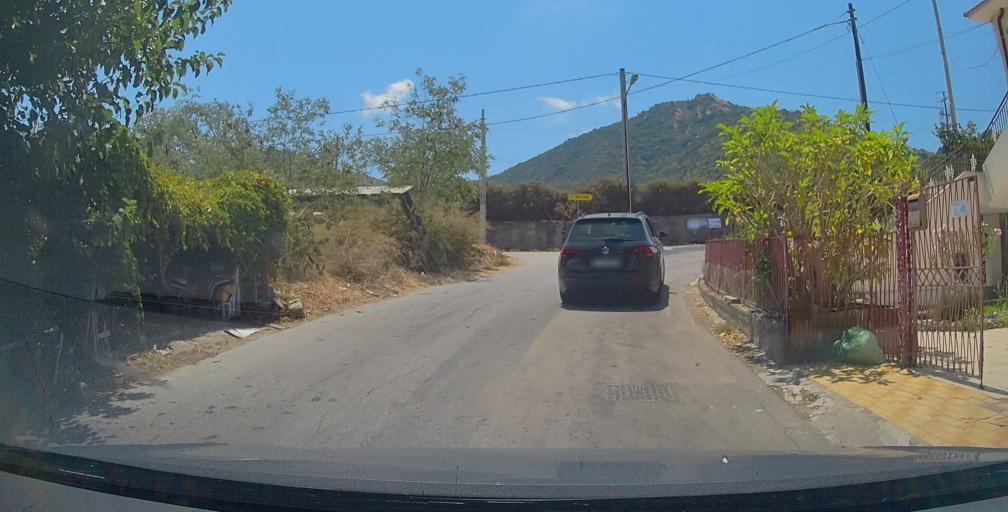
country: IT
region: Sicily
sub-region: Messina
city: Oliveri
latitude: 38.1455
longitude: 15.0153
